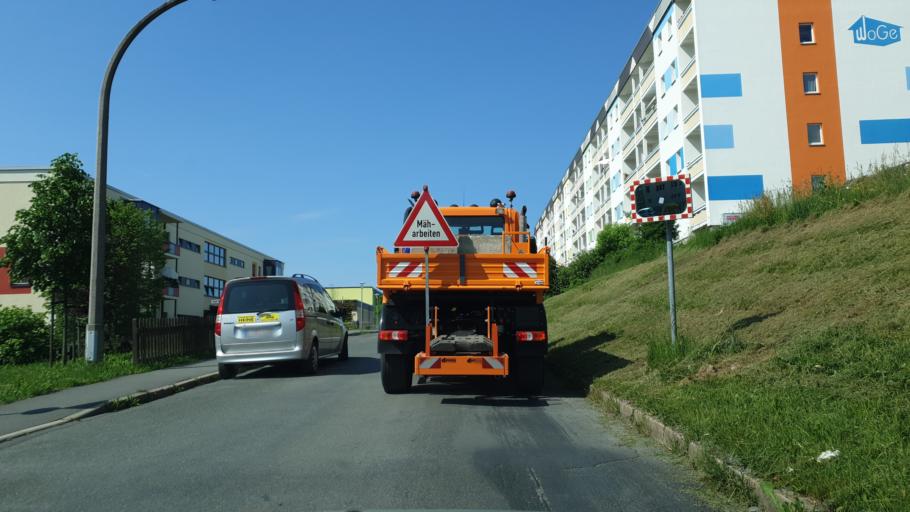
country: DE
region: Saxony
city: Klingenthal
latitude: 50.3612
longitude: 12.4543
